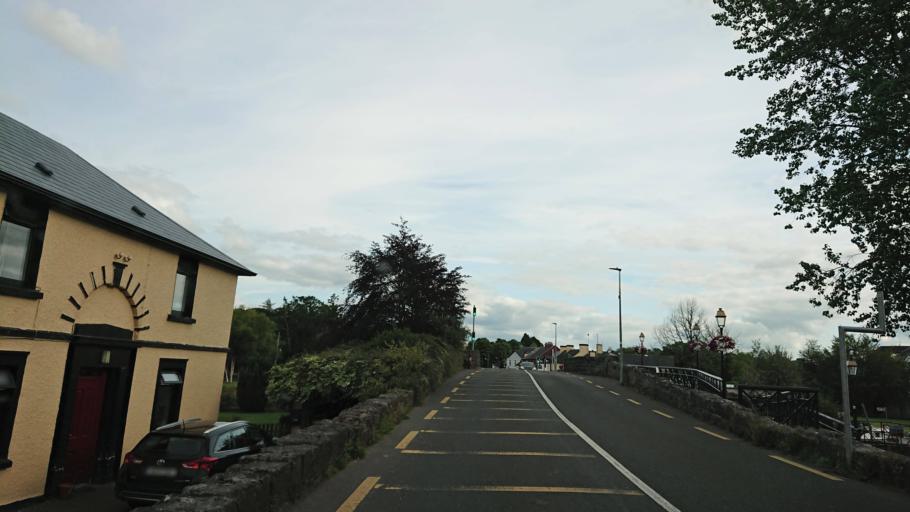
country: IE
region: Connaught
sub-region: County Leitrim
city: Carrick-on-Shannon
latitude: 53.9909
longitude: -8.0654
